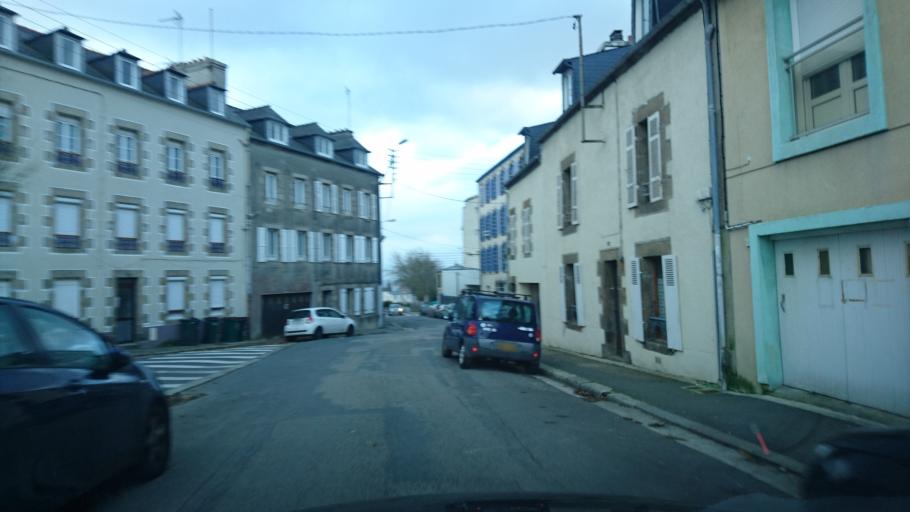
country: FR
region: Brittany
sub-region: Departement du Finistere
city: Brest
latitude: 48.3949
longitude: -4.4716
